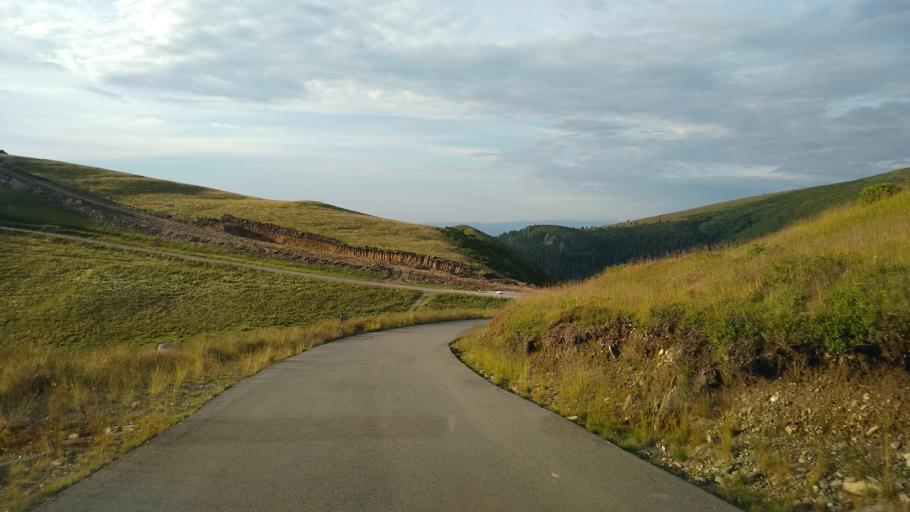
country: RO
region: Hunedoara
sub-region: Municipiul  Vulcan
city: Jiu-Paroseni
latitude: 45.3082
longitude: 23.3119
